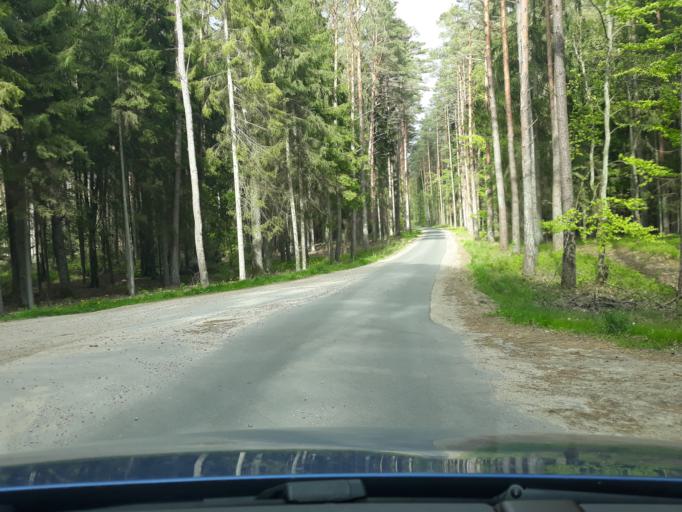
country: PL
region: Pomeranian Voivodeship
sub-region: Powiat czluchowski
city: Czluchow
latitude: 53.7426
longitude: 17.3503
